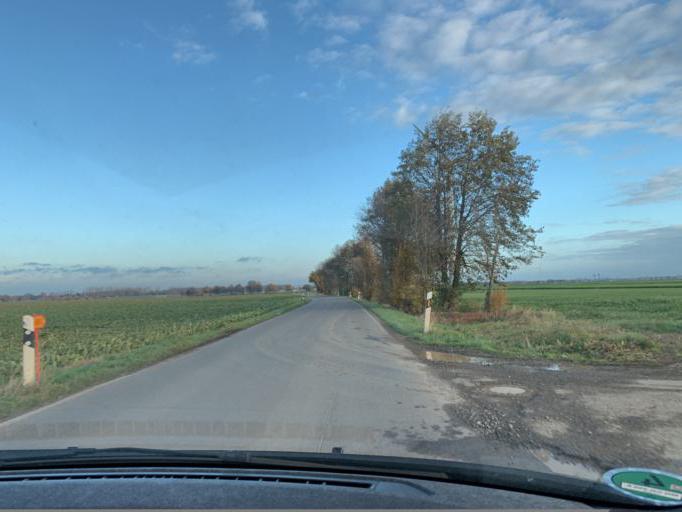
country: DE
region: North Rhine-Westphalia
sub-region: Regierungsbezirk Koln
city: Titz
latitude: 51.0641
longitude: 6.4075
